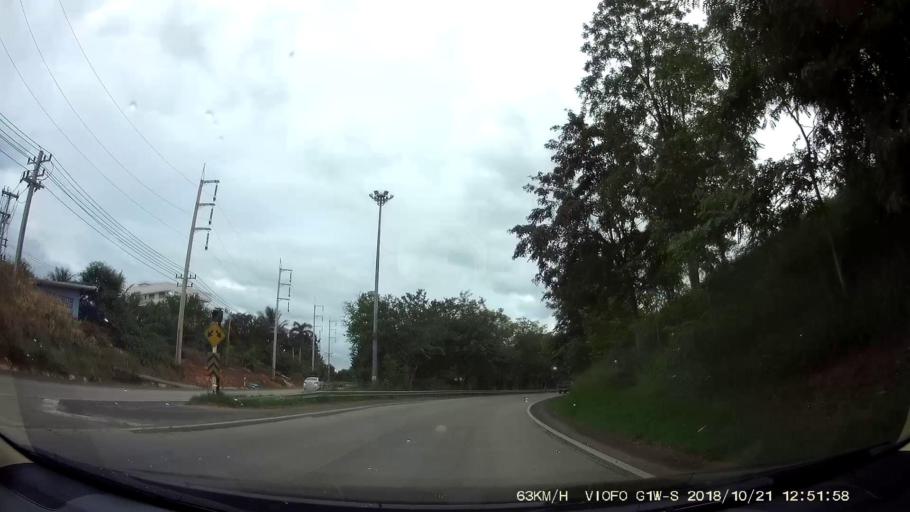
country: TH
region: Nakhon Ratchasima
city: Amphoe Sikhiu
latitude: 14.8638
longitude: 101.6987
